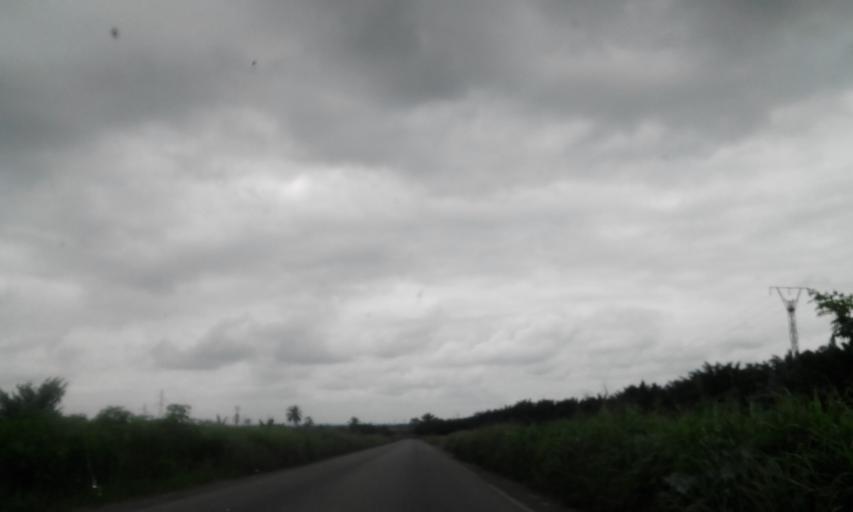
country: CI
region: Sud-Comoe
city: Adiake
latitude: 5.3965
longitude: -3.3912
